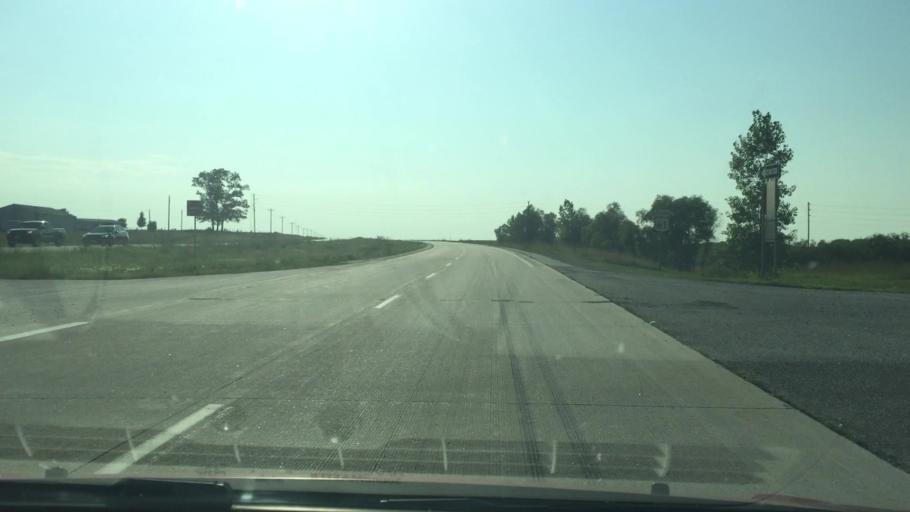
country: US
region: Iowa
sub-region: Scott County
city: Blue Grass
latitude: 41.5193
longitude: -90.8557
